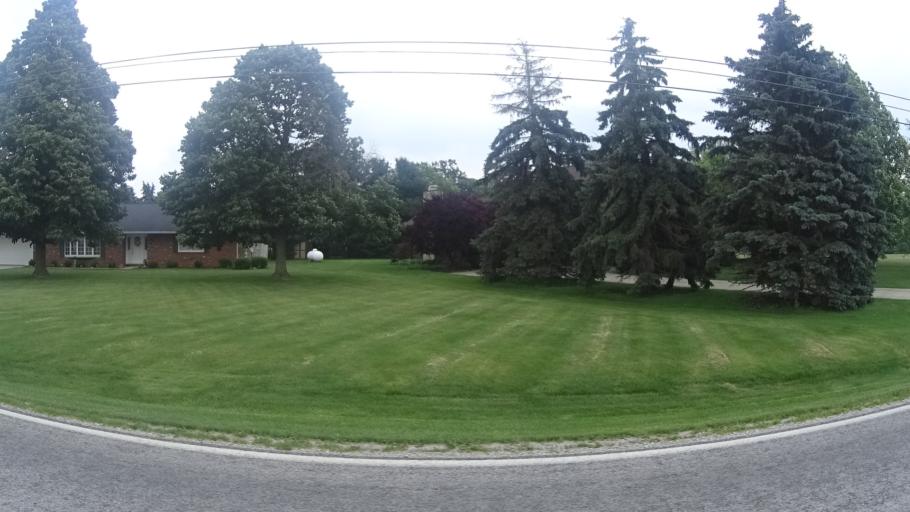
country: US
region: Ohio
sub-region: Erie County
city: Milan
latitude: 41.3299
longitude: -82.6275
